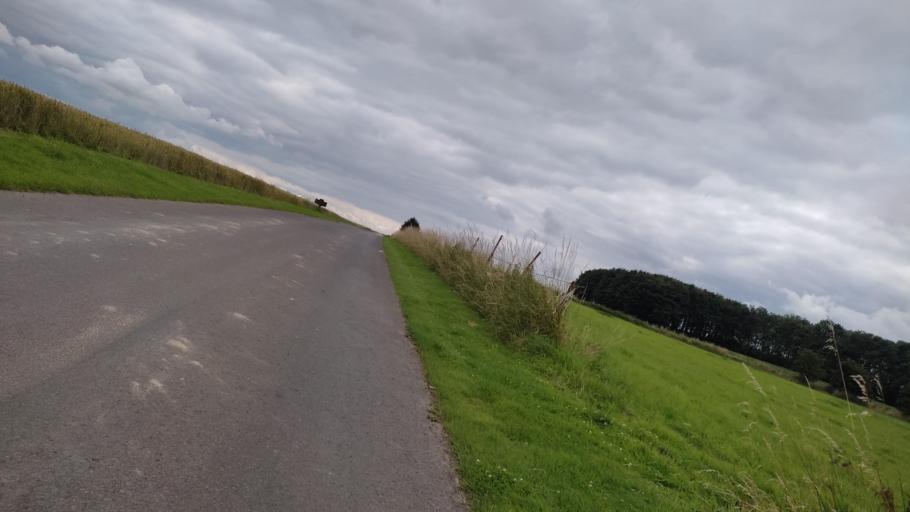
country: FR
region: Nord-Pas-de-Calais
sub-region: Departement du Pas-de-Calais
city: Beaumetz-les-Loges
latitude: 50.2363
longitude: 2.6291
